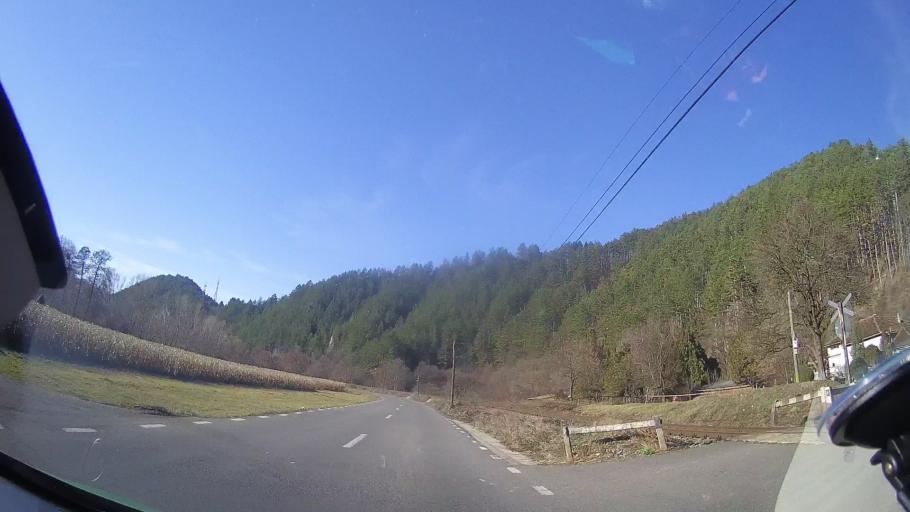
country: RO
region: Bihor
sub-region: Comuna Bratca
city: Bratca
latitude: 46.9299
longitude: 22.6376
